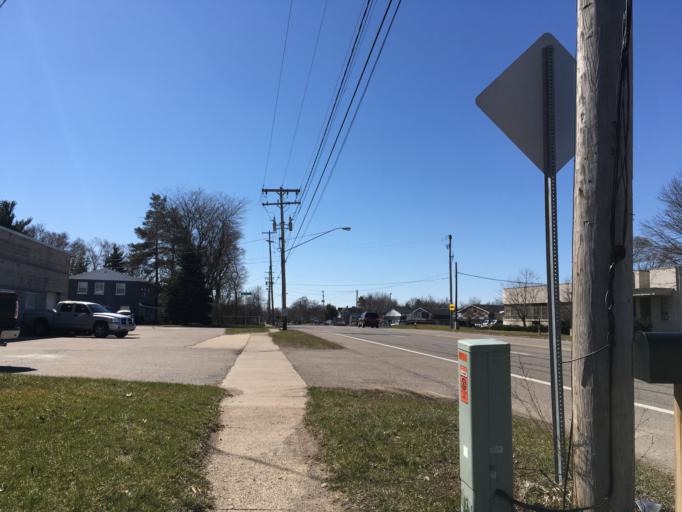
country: US
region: Michigan
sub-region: Kalamazoo County
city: Portage
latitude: 42.1760
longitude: -85.5674
